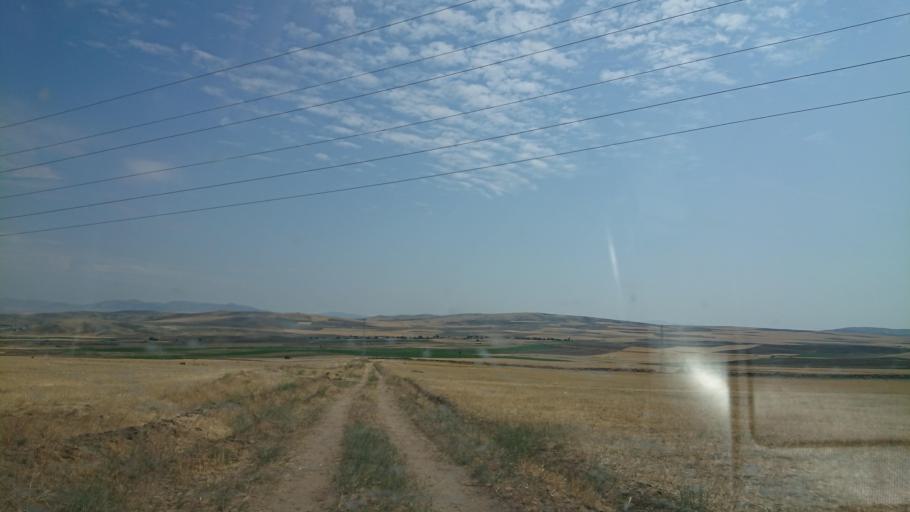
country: TR
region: Aksaray
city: Sariyahsi
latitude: 38.9526
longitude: 33.9105
